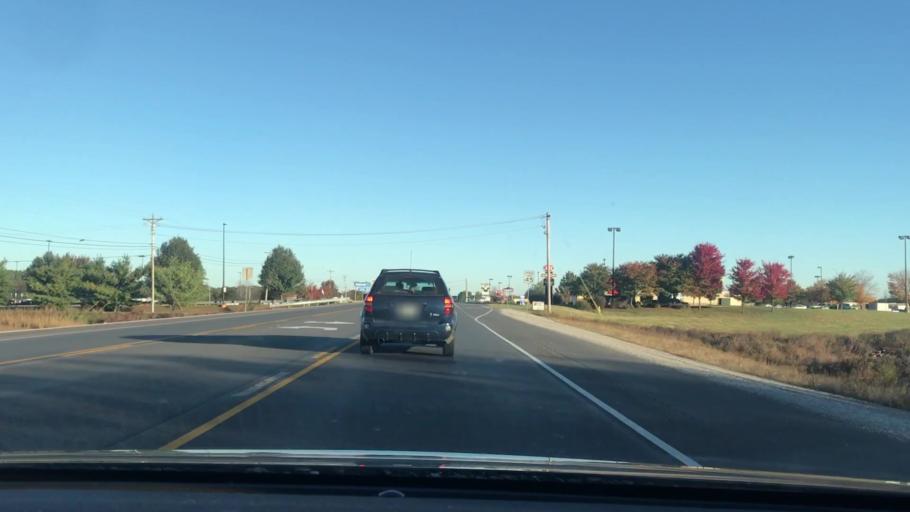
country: US
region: Kentucky
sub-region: Simpson County
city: Franklin
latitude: 36.6937
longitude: -86.5699
